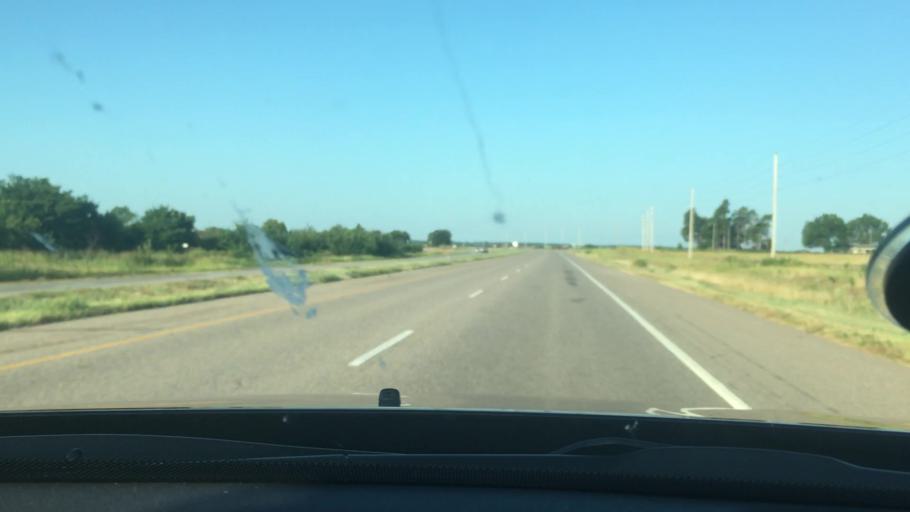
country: US
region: Oklahoma
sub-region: Pontotoc County
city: Ada
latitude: 34.7197
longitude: -96.7186
